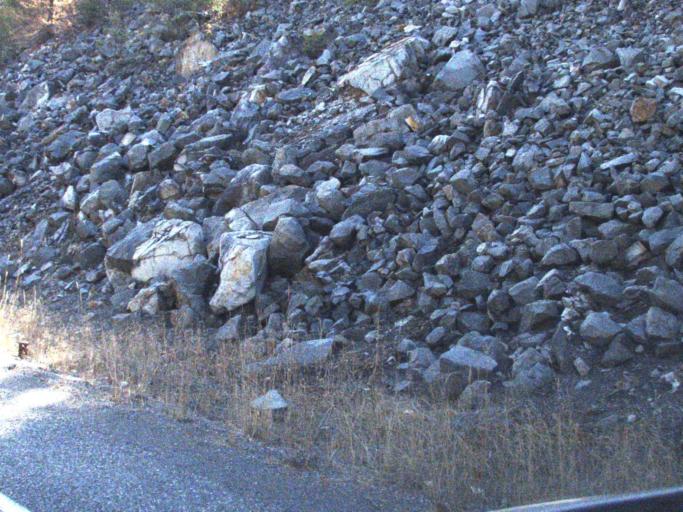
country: US
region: Washington
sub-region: Ferry County
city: Republic
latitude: 48.6517
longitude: -118.7877
